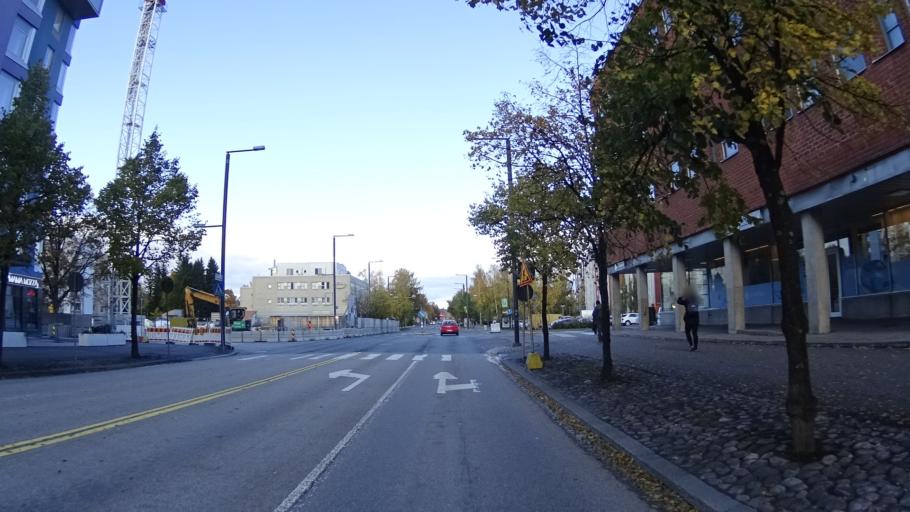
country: FI
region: Uusimaa
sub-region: Helsinki
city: Vantaa
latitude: 60.2902
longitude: 25.0360
